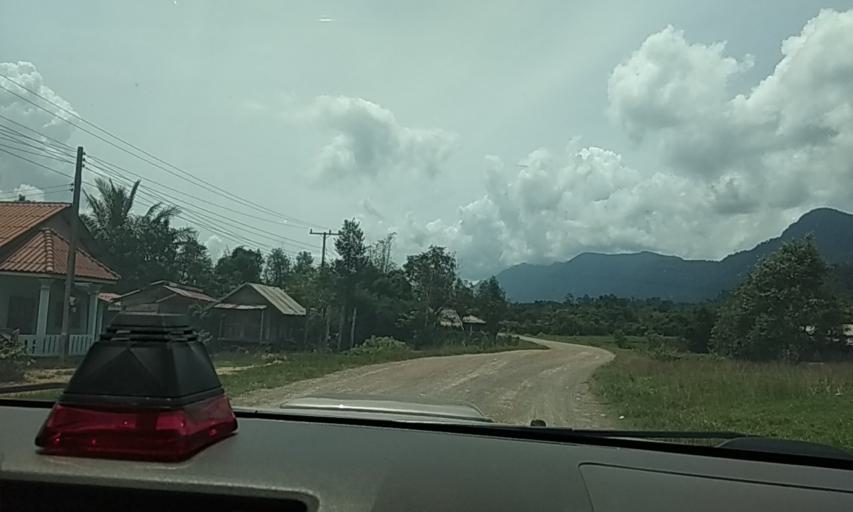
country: LA
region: Bolikhamxai
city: Ban Nahin
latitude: 18.1532
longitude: 104.7230
